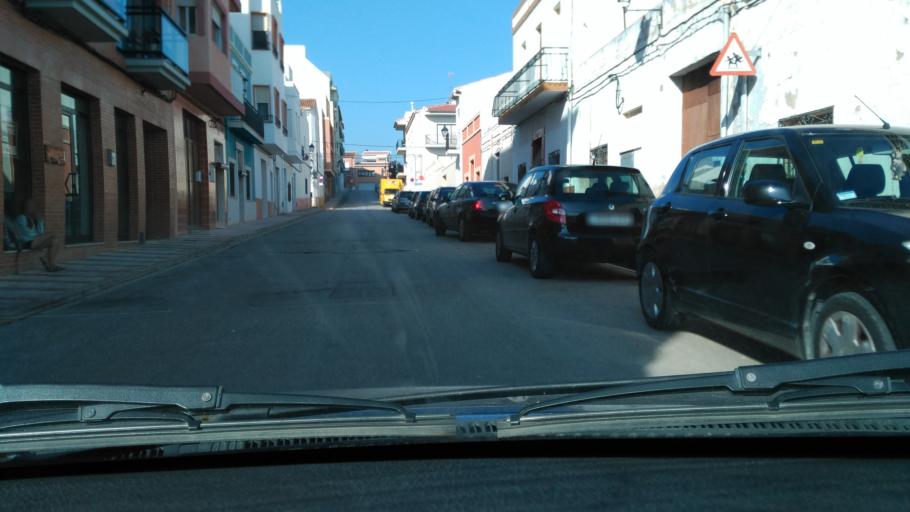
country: ES
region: Valencia
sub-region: Provincia de Alicante
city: Gata de Gorgos
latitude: 38.7712
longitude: 0.0849
